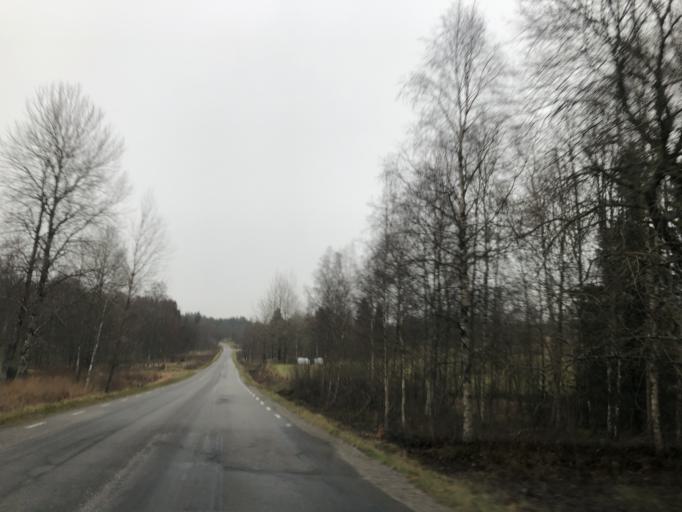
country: SE
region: Vaestra Goetaland
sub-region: Ulricehamns Kommun
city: Ulricehamn
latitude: 57.7182
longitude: 13.5286
